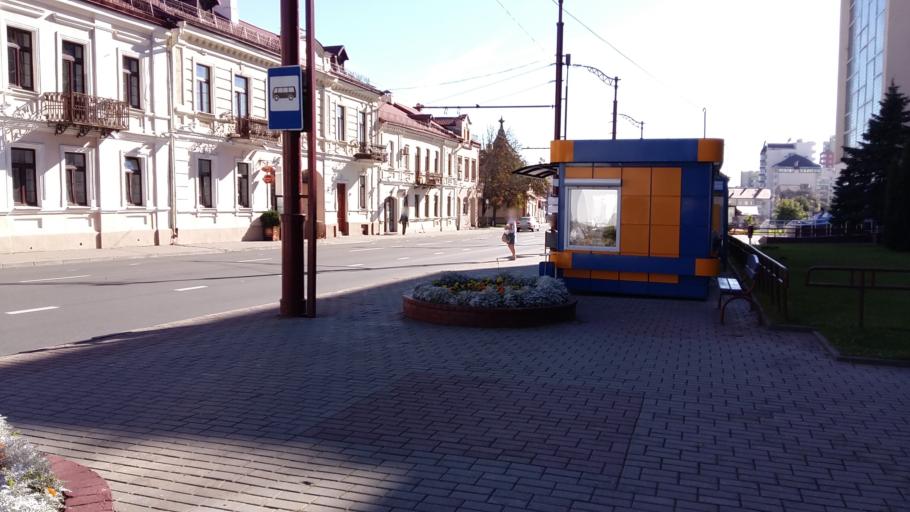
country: BY
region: Grodnenskaya
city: Hrodna
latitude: 53.6769
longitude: 23.8377
